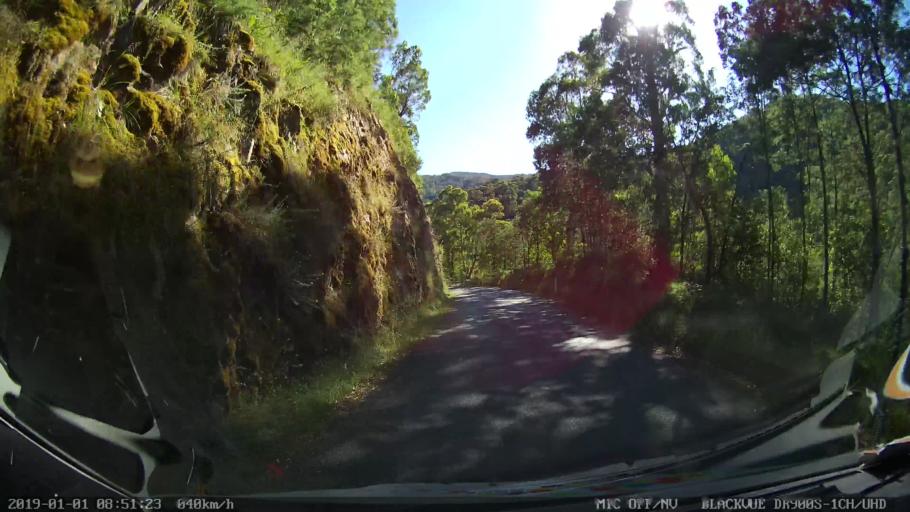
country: AU
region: New South Wales
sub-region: Snowy River
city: Jindabyne
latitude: -36.2714
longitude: 148.2007
